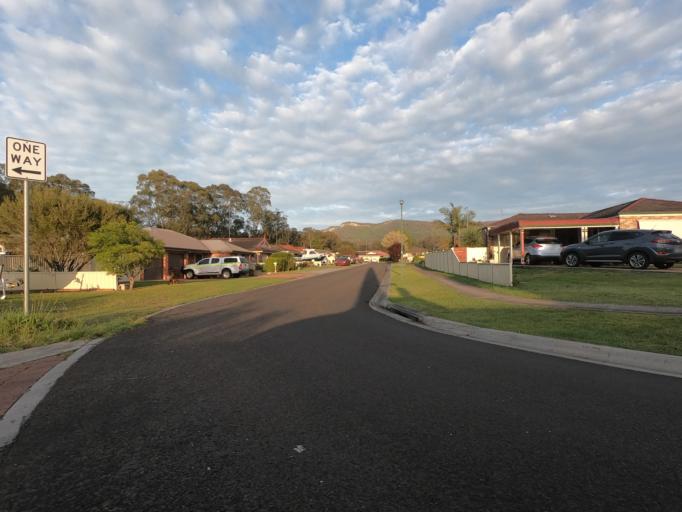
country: AU
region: New South Wales
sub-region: Wollongong
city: Dapto
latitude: -34.4953
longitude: 150.7706
